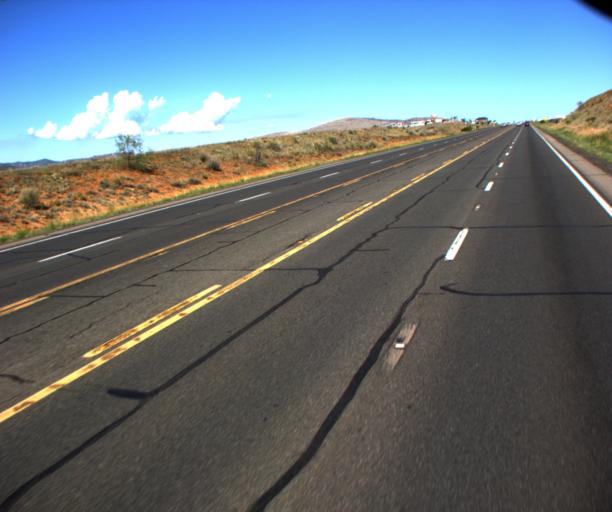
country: US
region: Arizona
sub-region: Yavapai County
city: Prescott Valley
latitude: 34.5816
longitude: -112.3039
